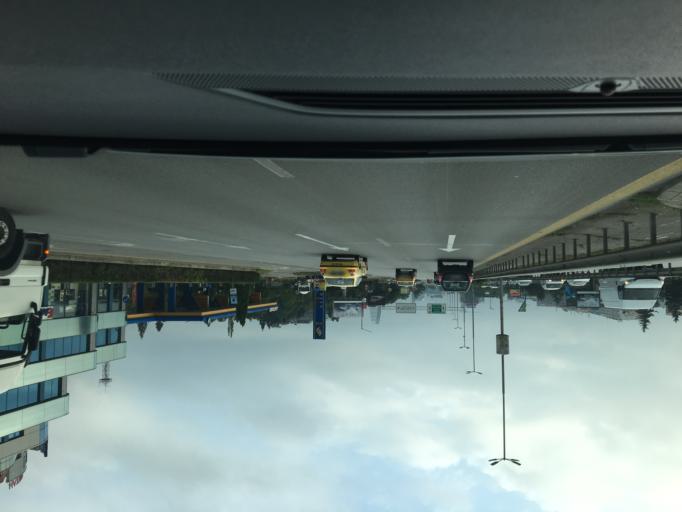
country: BG
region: Sofia-Capital
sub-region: Stolichna Obshtina
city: Sofia
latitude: 42.6584
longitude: 23.3827
